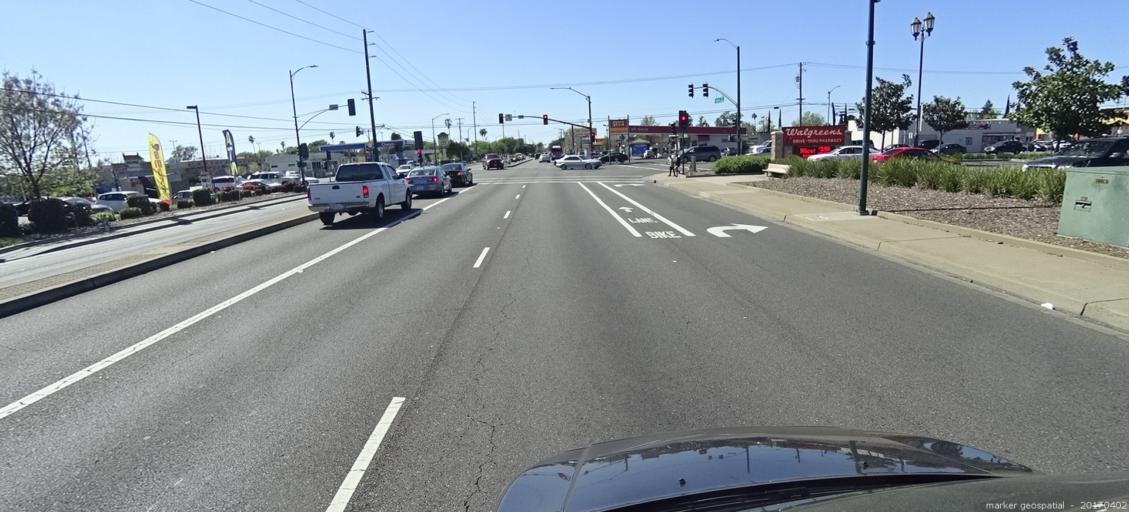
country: US
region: California
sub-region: Sacramento County
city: Parkway
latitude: 38.4958
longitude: -121.4820
